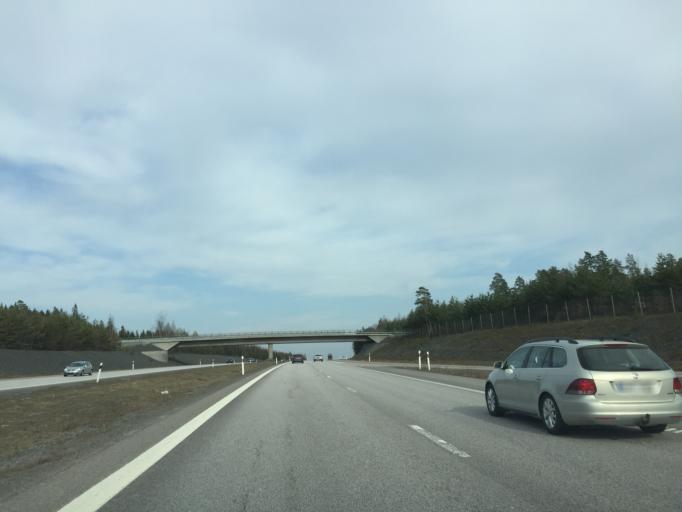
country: SE
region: Vaestmanland
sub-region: Arboga Kommun
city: Arboga
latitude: 59.3999
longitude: 15.7196
